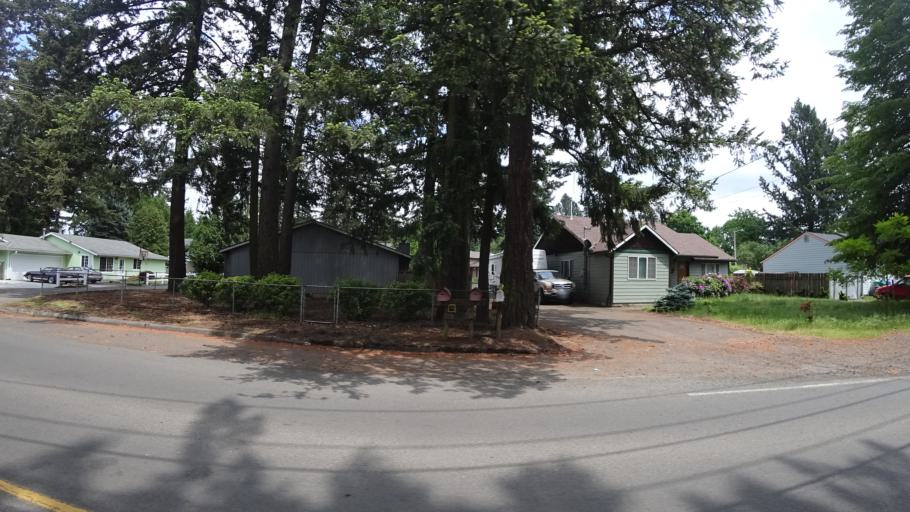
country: US
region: Oregon
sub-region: Multnomah County
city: Fairview
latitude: 45.5156
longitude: -122.4846
